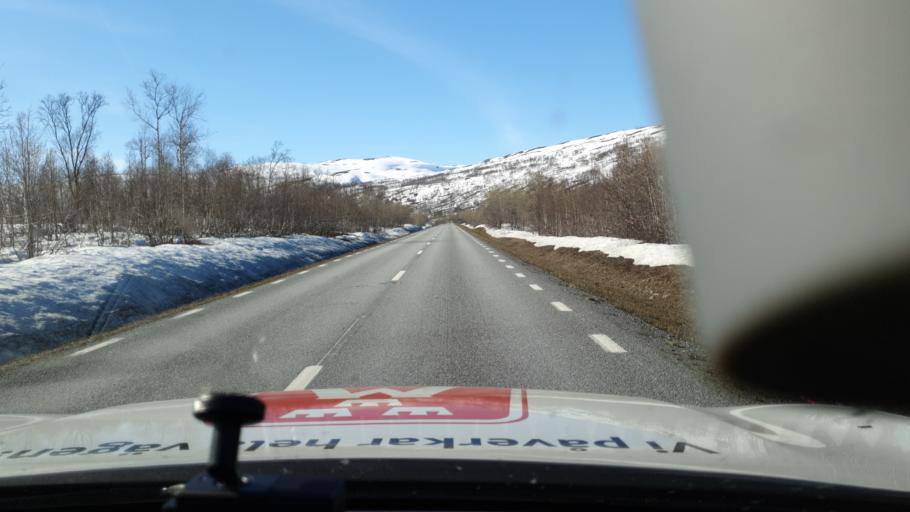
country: NO
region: Nordland
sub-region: Rana
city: Mo i Rana
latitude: 66.1144
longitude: 14.8097
